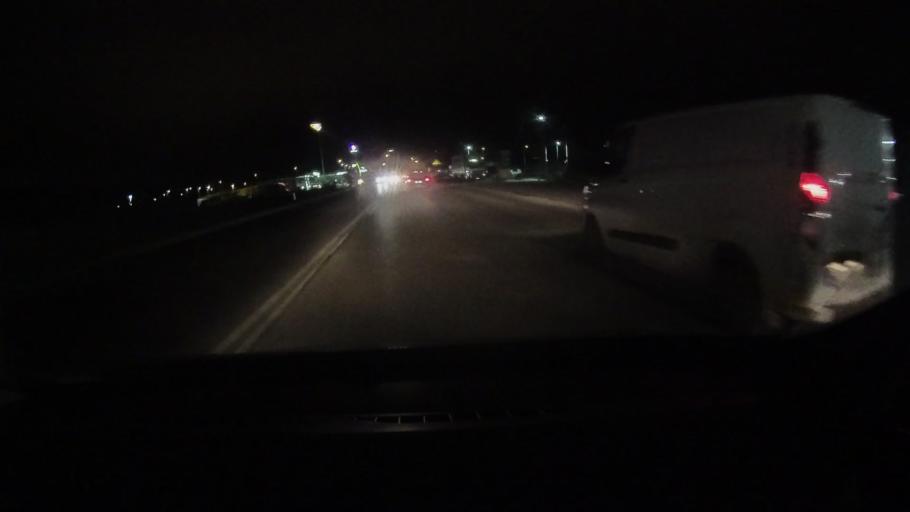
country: RO
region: Brasov
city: Brasov
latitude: 45.6967
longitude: 25.5828
